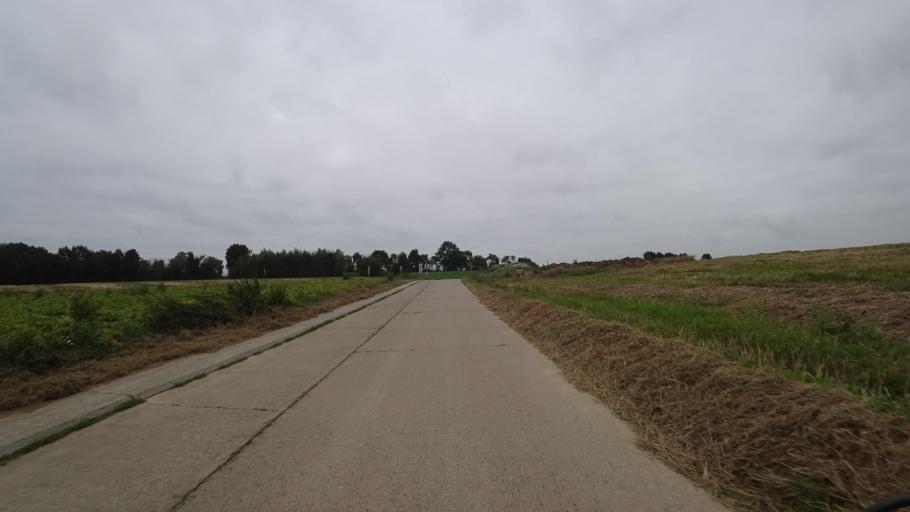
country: BE
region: Wallonia
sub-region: Province du Brabant Wallon
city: Mont-Saint-Guibert
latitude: 50.6400
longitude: 4.6325
